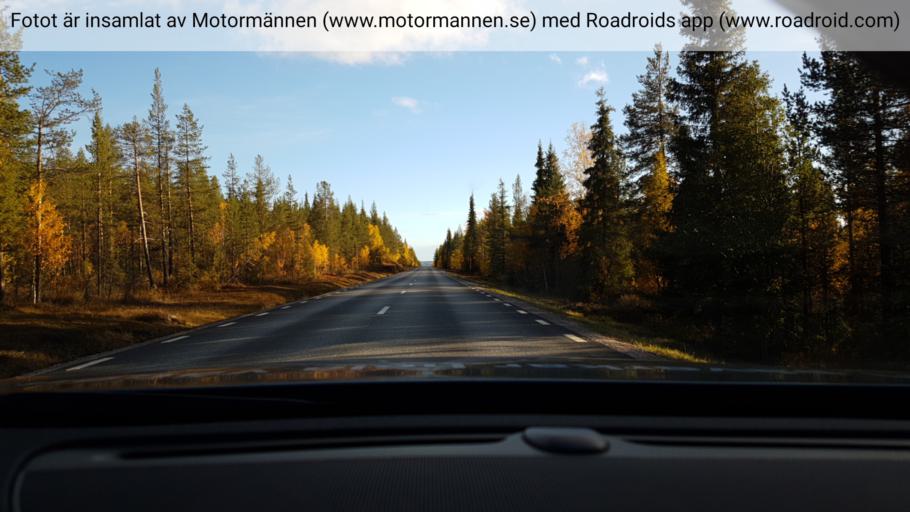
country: SE
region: Norrbotten
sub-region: Jokkmokks Kommun
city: Jokkmokk
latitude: 66.9031
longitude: 19.8270
